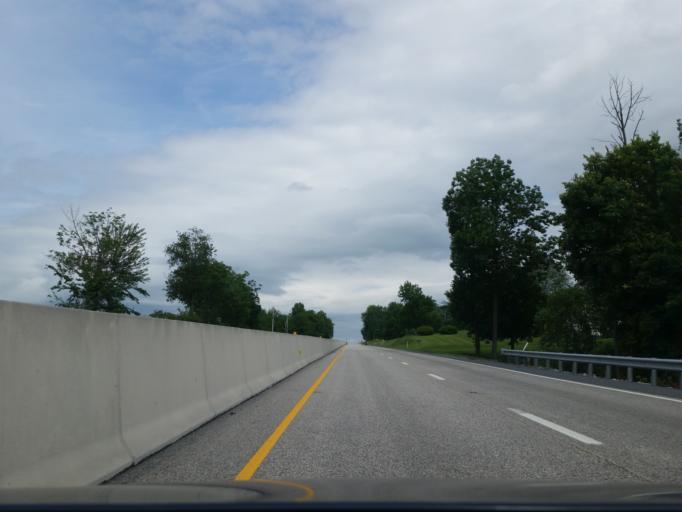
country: US
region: Pennsylvania
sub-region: Lebanon County
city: Jonestown
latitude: 40.4065
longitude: -76.5454
